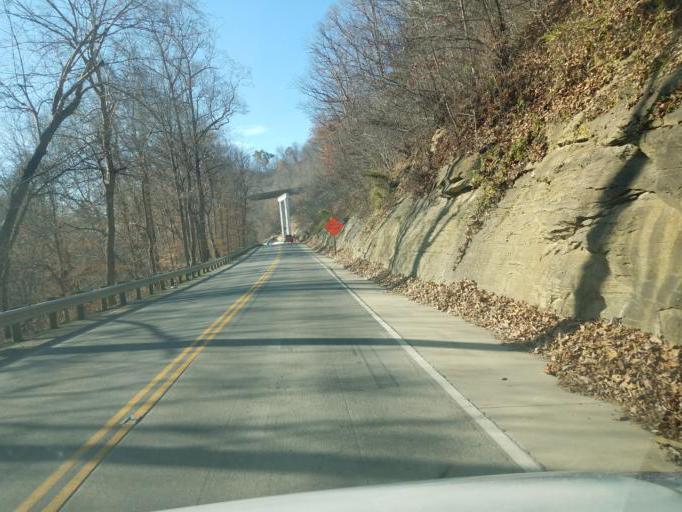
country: US
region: Ohio
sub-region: Scioto County
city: Sciotodale
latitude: 38.7750
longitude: -82.8702
